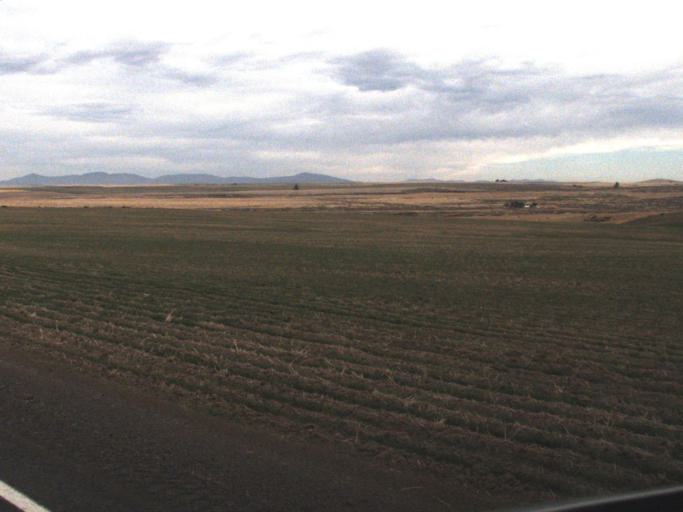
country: US
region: Washington
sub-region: Okanogan County
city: Coulee Dam
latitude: 47.6536
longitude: -118.7212
